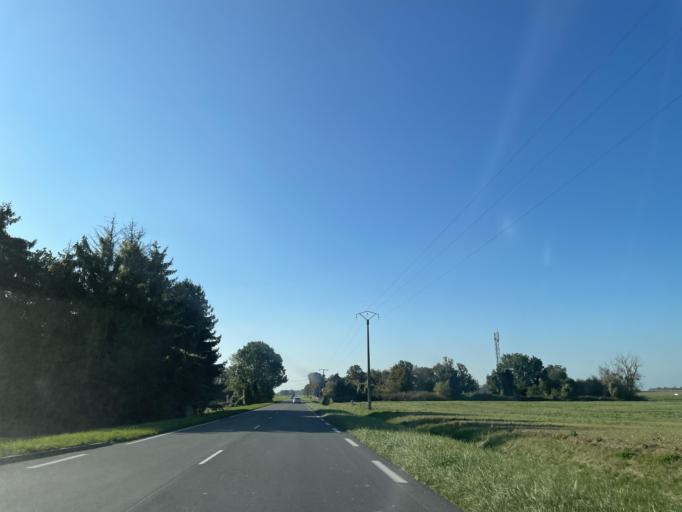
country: FR
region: Ile-de-France
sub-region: Departement de Seine-et-Marne
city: Pommeuse
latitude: 48.8312
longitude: 3.0139
